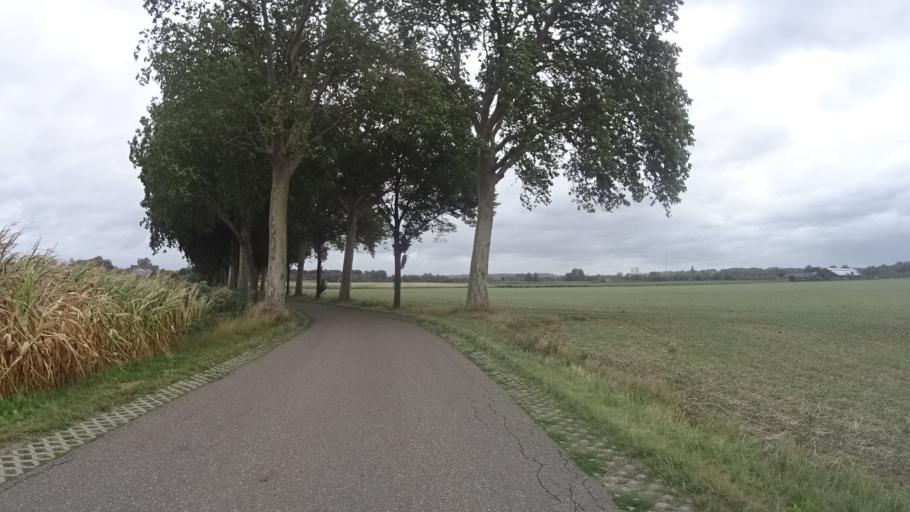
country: NL
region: Limburg
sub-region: Eijsden-Margraten
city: Eijsden
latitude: 50.7645
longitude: 5.6960
